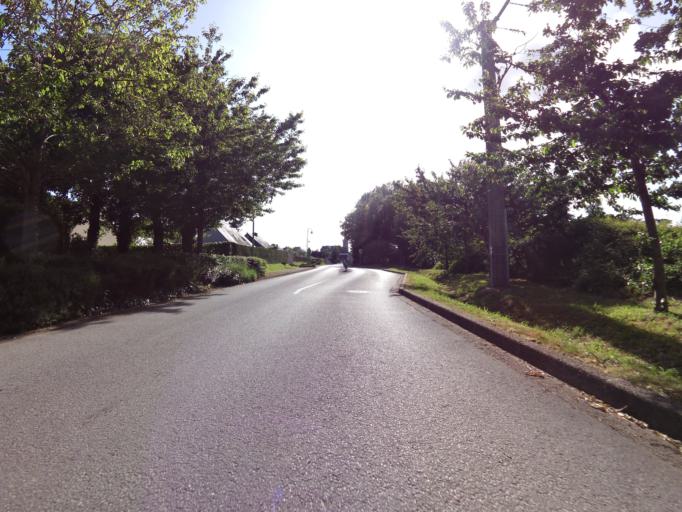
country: FR
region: Brittany
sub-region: Departement du Morbihan
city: Pluherlin
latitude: 47.6970
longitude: -2.3584
